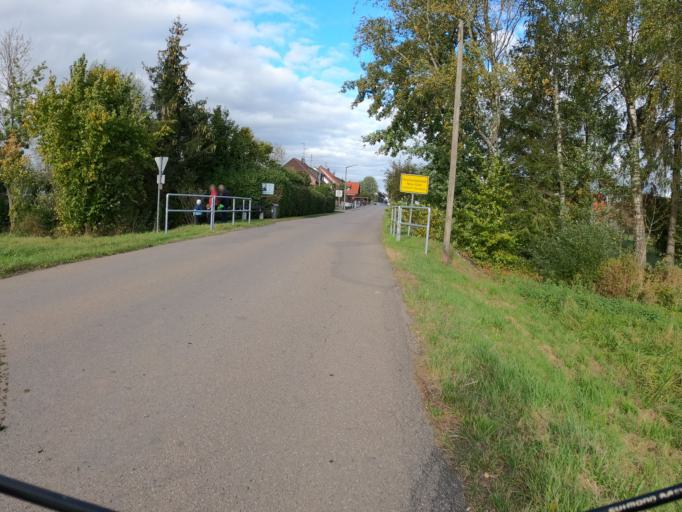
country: DE
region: Bavaria
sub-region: Swabia
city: Holzheim
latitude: 48.3990
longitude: 10.1013
